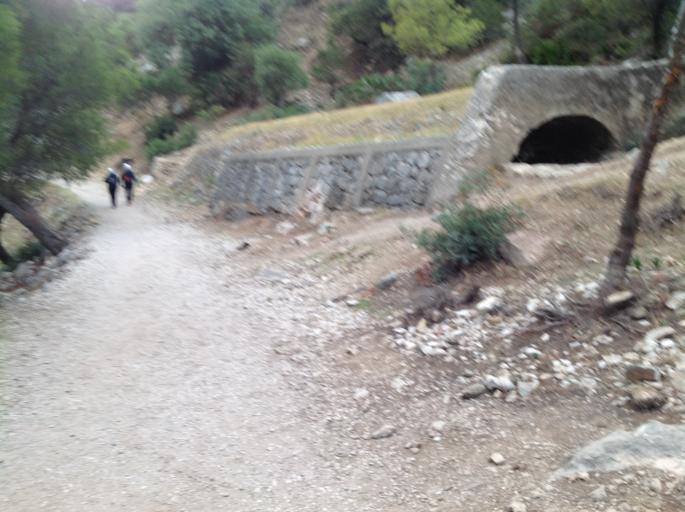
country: ES
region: Andalusia
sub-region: Provincia de Malaga
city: Carratraca
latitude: 36.9218
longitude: -4.7806
